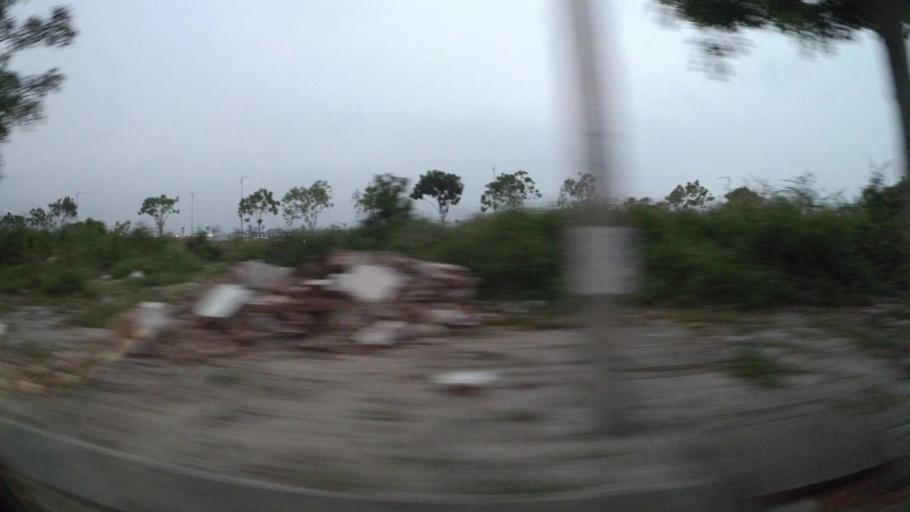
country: VN
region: Da Nang
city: Ngu Hanh Son
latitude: 16.0348
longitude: 108.2389
